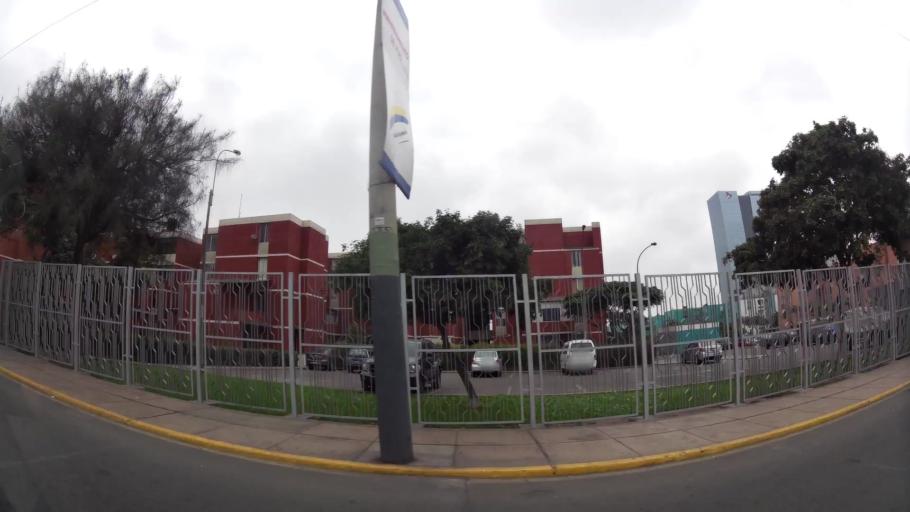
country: PE
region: Lima
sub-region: Lima
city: San Luis
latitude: -12.0835
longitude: -76.9989
